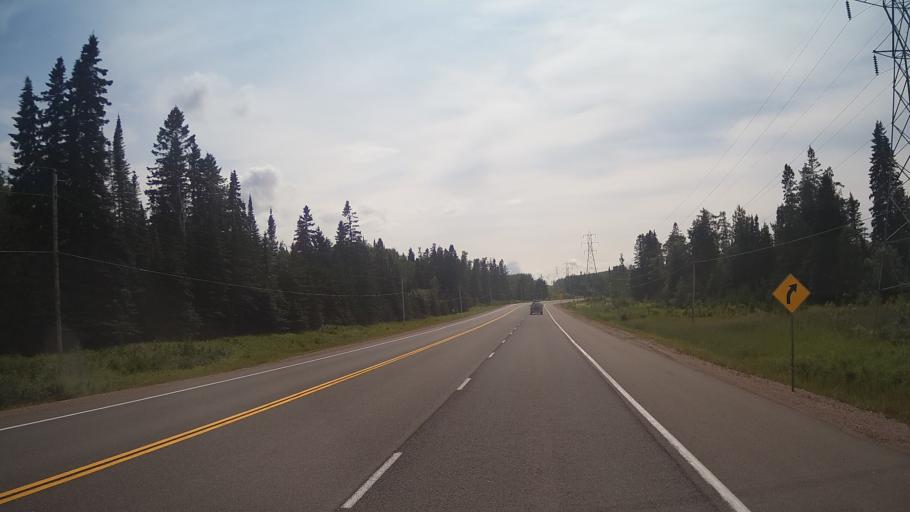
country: CA
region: Ontario
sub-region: Thunder Bay District
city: Thunder Bay
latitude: 48.6487
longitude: -88.7093
